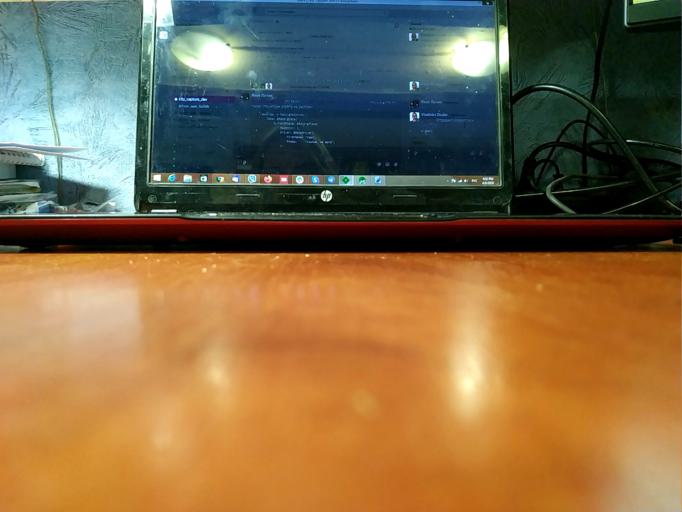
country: RU
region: Tverskaya
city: Sandovo
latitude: 58.5540
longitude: 36.3895
